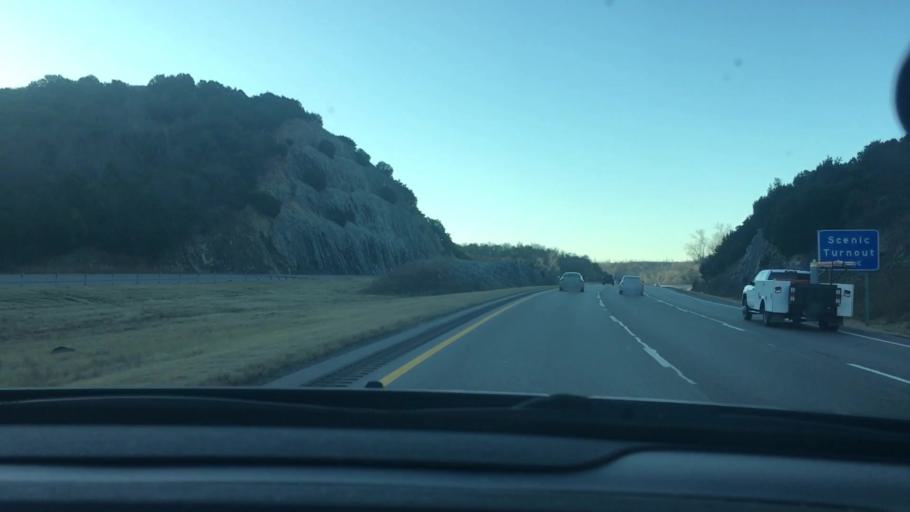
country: US
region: Oklahoma
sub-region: Murray County
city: Davis
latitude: 34.4422
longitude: -97.1289
